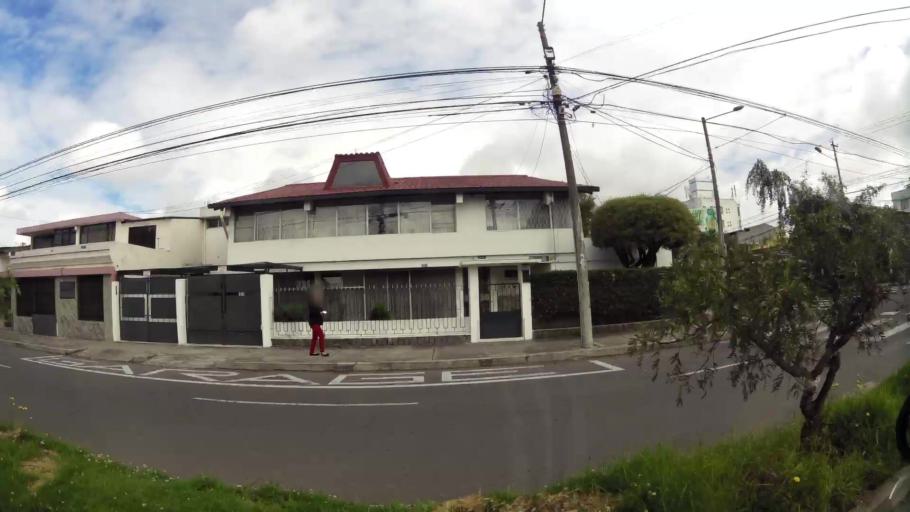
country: EC
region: Pichincha
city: Quito
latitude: -0.1656
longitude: -78.4769
